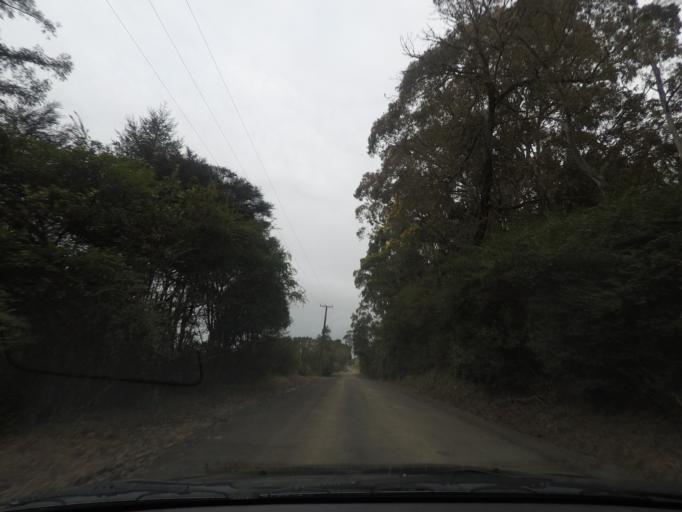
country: NZ
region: Auckland
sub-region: Auckland
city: Muriwai Beach
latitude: -36.7551
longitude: 174.5752
